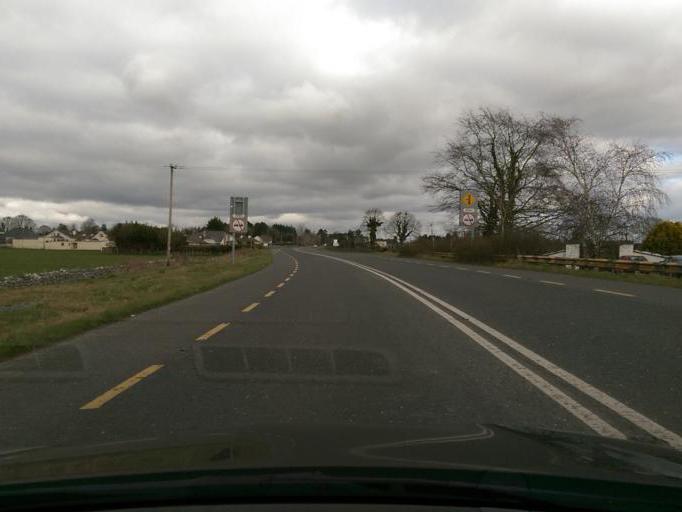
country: IE
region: Connaught
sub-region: County Galway
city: Ballinasloe
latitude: 53.3290
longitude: -8.1594
